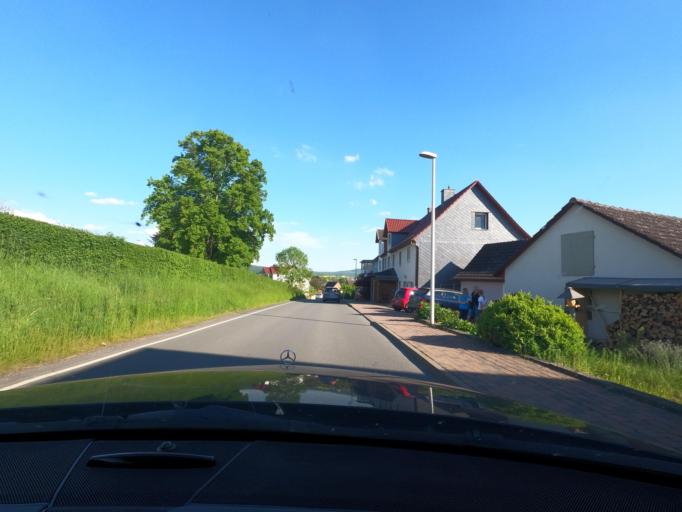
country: DE
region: Hesse
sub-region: Regierungsbezirk Kassel
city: Wolfhagen
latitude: 51.3430
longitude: 9.2296
